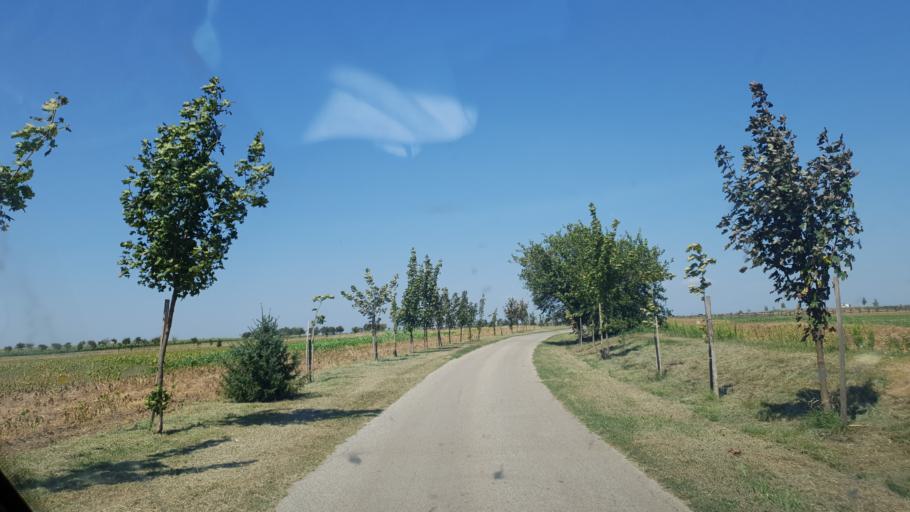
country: RS
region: Autonomna Pokrajina Vojvodina
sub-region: Juznobacki Okrug
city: Kovilj
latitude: 45.2080
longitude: 20.0629
